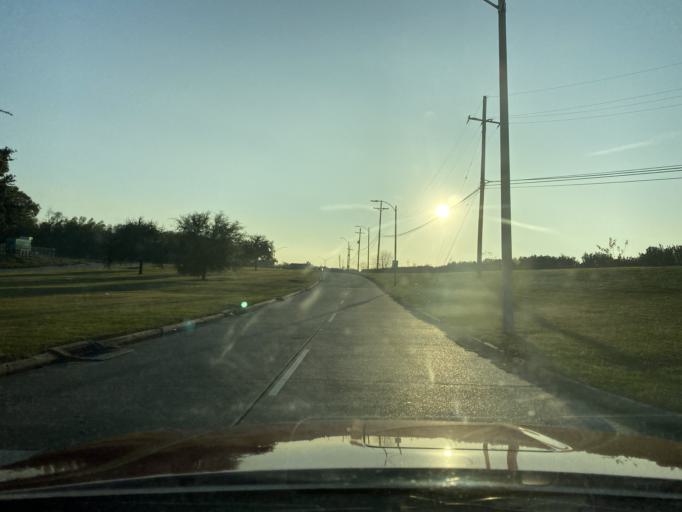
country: US
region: Louisiana
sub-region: Orleans Parish
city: New Orleans
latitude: 30.0289
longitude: -90.0458
